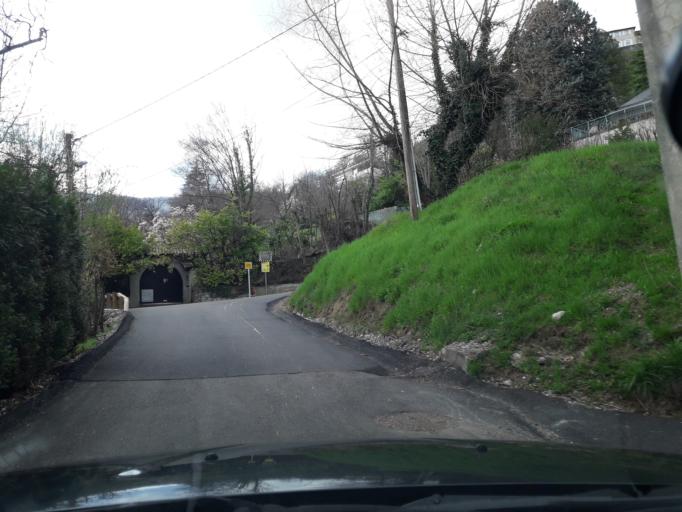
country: FR
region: Rhone-Alpes
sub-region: Departement de l'Isere
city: Corenc
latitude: 45.2191
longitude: 5.7685
